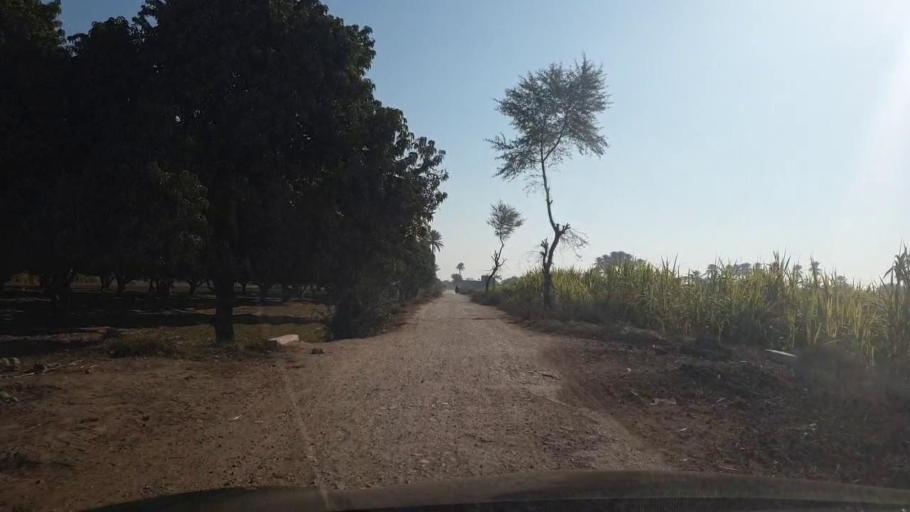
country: PK
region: Sindh
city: Ghotki
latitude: 27.9946
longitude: 69.3196
